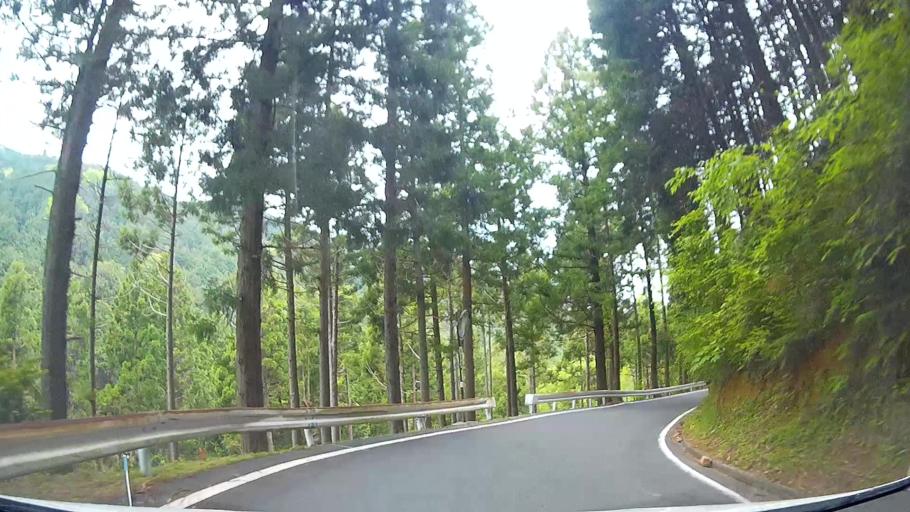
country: JP
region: Shizuoka
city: Ito
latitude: 34.9097
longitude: 139.0515
